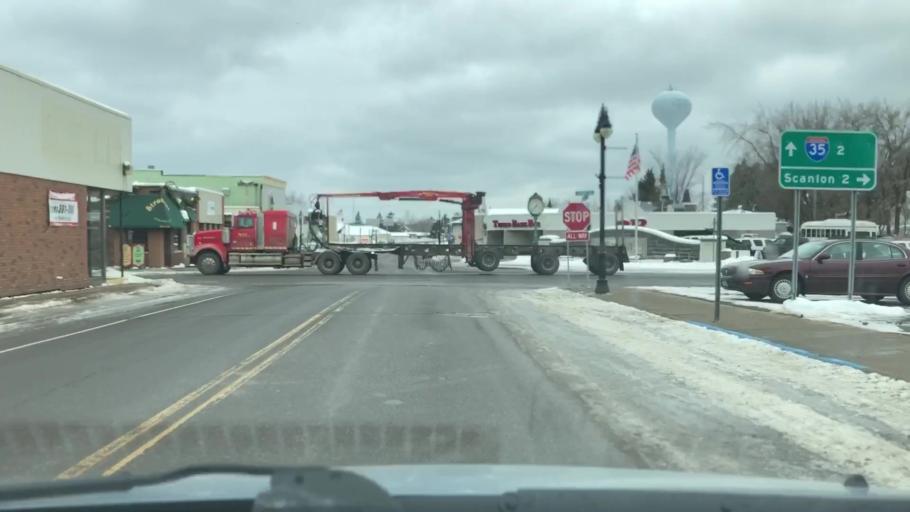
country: US
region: Minnesota
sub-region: Carlton County
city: Carlton
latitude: 46.6640
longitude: -92.4244
